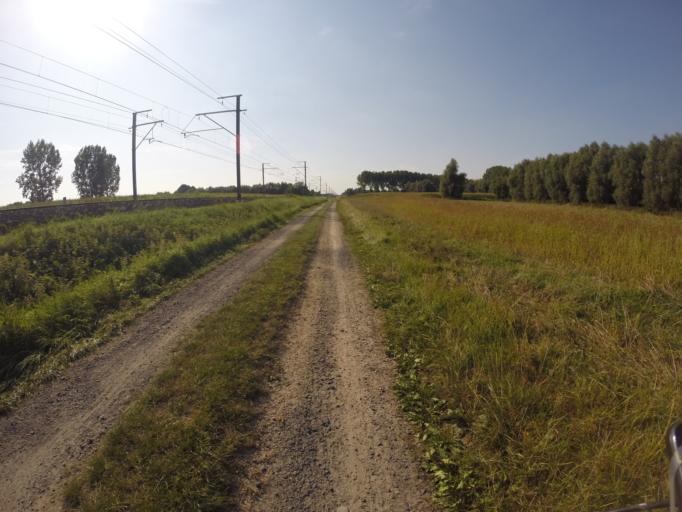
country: BE
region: Flanders
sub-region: Provincie Oost-Vlaanderen
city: Nevele
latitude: 51.0761
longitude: 3.5228
